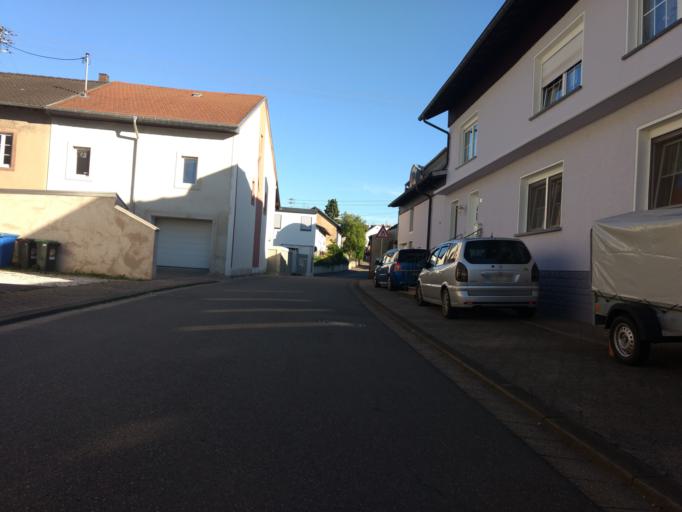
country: DE
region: Saarland
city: Merzig
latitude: 49.4044
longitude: 6.6484
